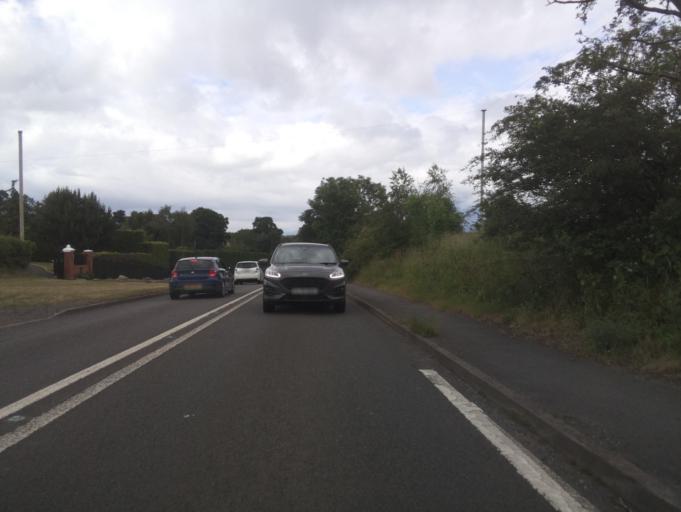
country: GB
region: England
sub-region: Dudley
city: Kingswinford
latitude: 52.4654
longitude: -2.1998
